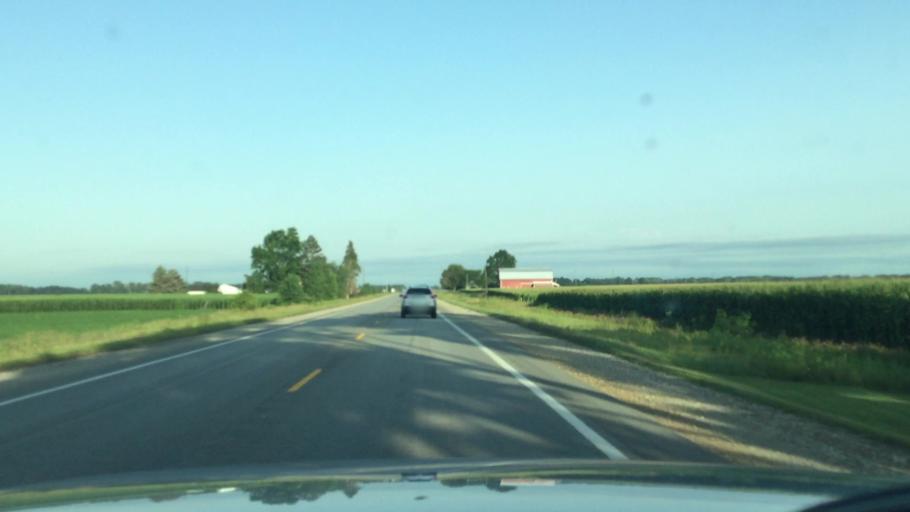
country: US
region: Michigan
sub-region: Montcalm County
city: Carson City
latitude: 43.1764
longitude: -84.7662
